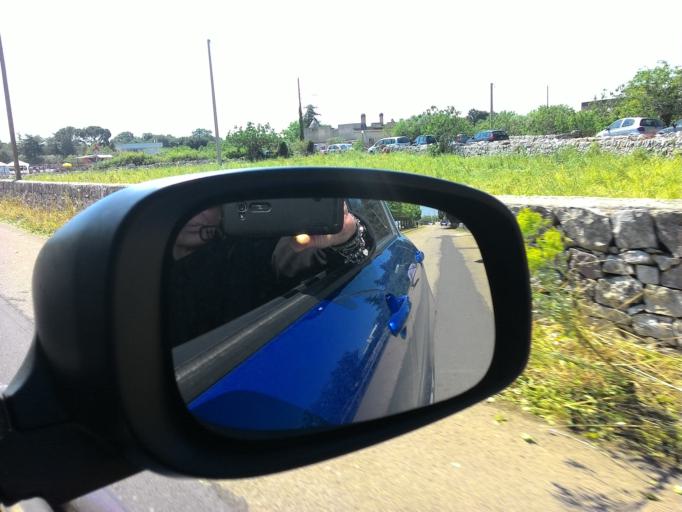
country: IT
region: Apulia
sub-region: Provincia di Bari
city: Putignano
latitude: 40.8479
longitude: 17.1439
